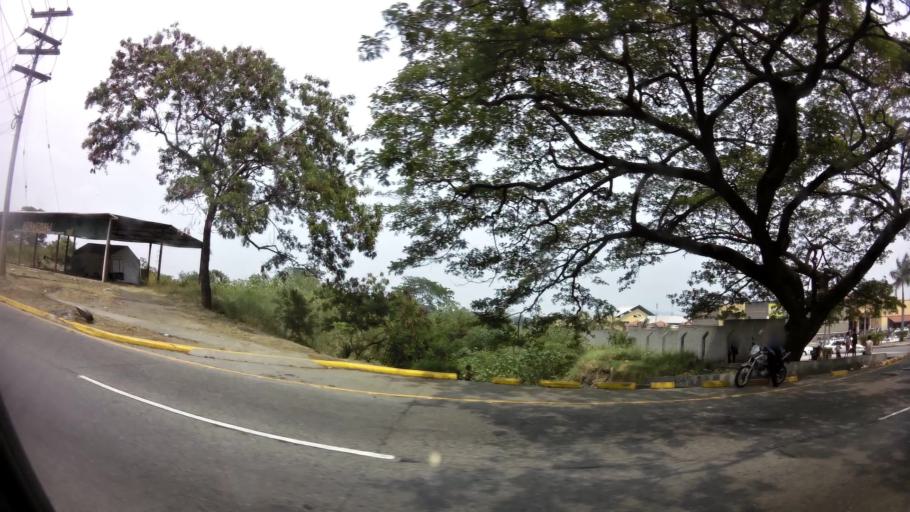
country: HN
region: Cortes
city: Armenta
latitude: 15.4733
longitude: -88.0337
